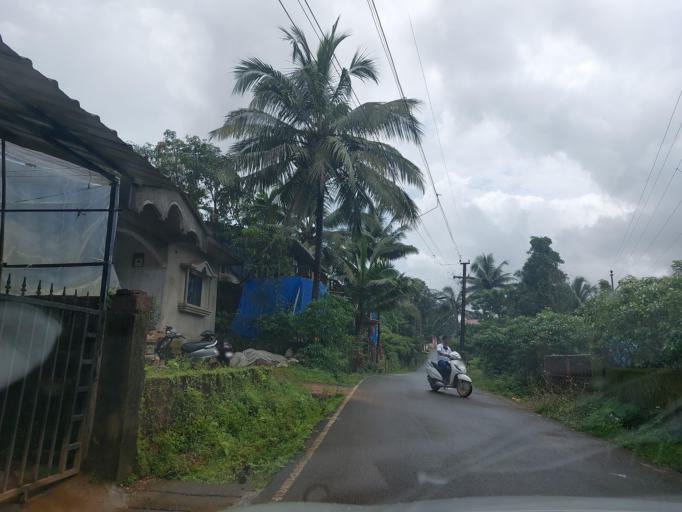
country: IN
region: Goa
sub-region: North Goa
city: Valpoy
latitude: 15.5384
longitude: 74.1420
